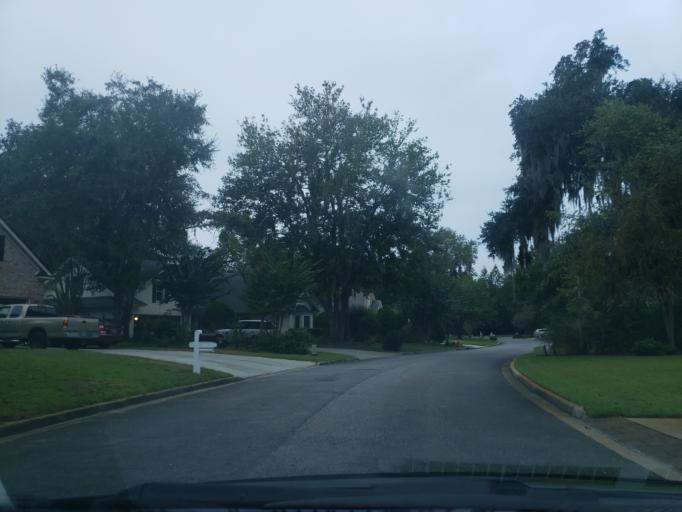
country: US
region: Georgia
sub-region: Chatham County
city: Isle of Hope
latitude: 31.9736
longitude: -81.0808
